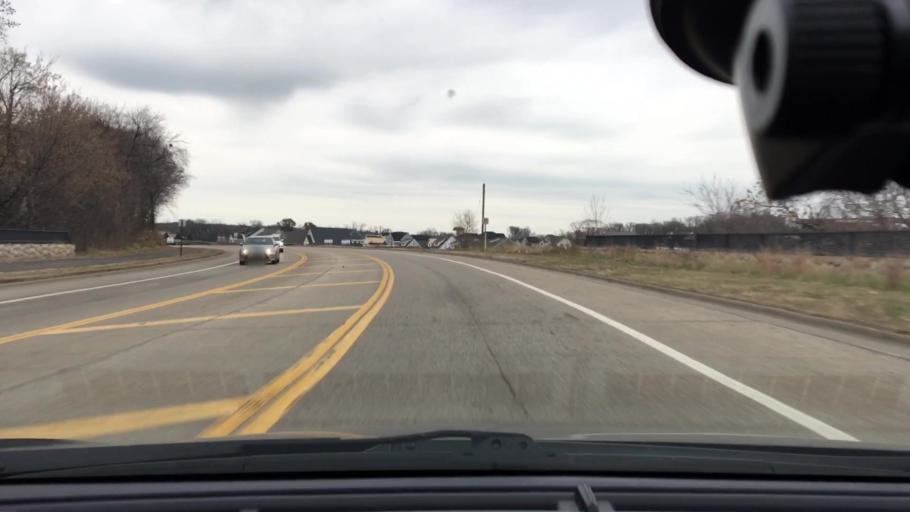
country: US
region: Minnesota
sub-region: Hennepin County
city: Corcoran
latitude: 45.0520
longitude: -93.5228
